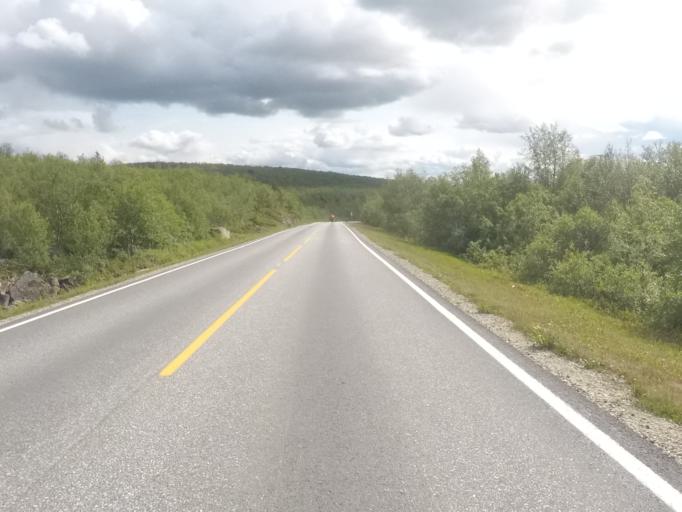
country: NO
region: Finnmark Fylke
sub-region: Karasjok
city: Karasjohka
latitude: 69.5111
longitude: 25.4671
